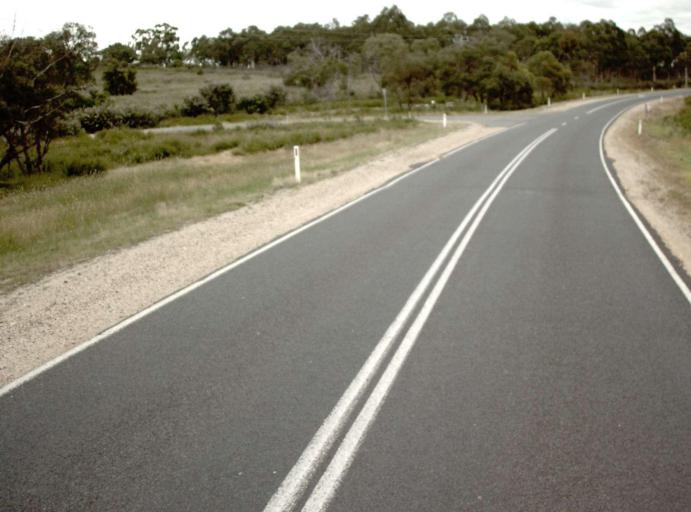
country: AU
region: Victoria
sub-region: Wellington
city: Sale
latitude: -38.1818
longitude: 147.1412
